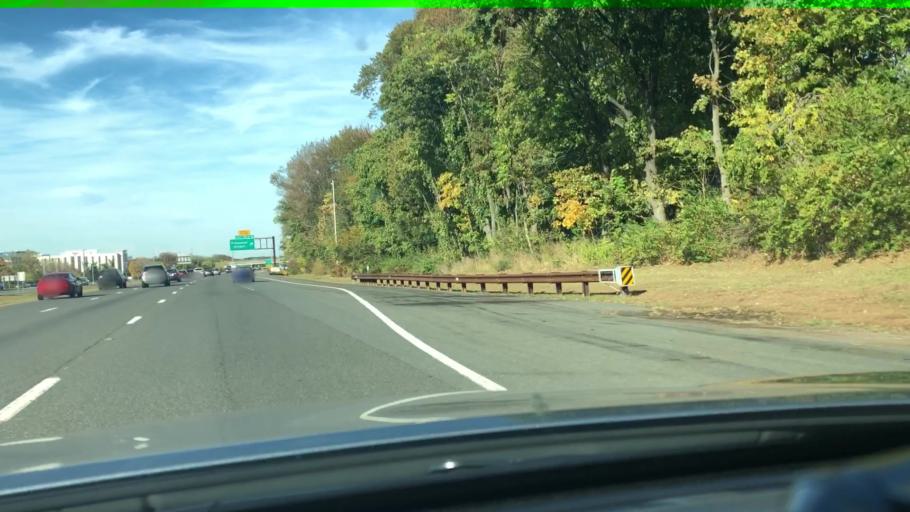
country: US
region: New Jersey
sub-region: Bergen County
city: Paramus
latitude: 40.9561
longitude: -74.0658
